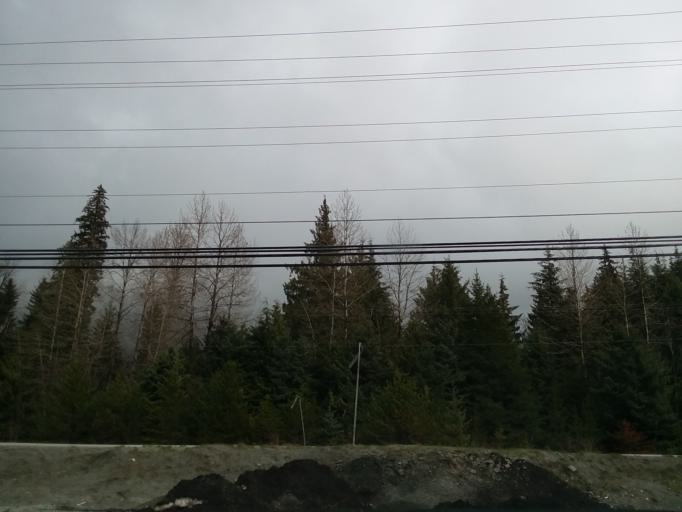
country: CA
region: British Columbia
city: Whistler
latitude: 50.1302
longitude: -122.9542
